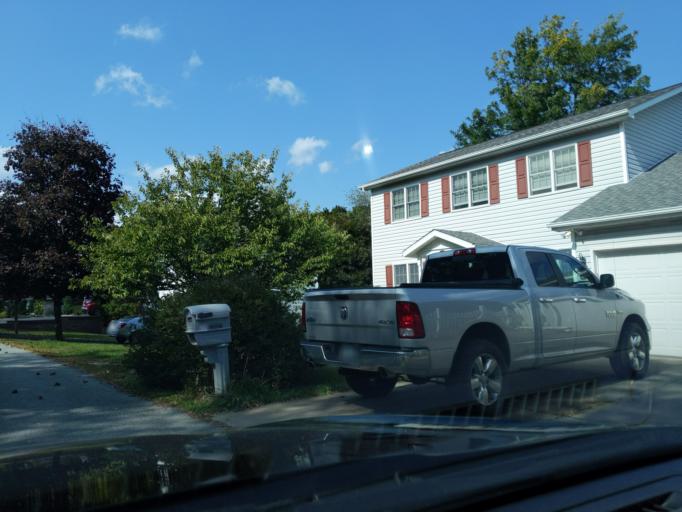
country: US
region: Pennsylvania
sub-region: Blair County
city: Altoona
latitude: 40.4979
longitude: -78.3999
